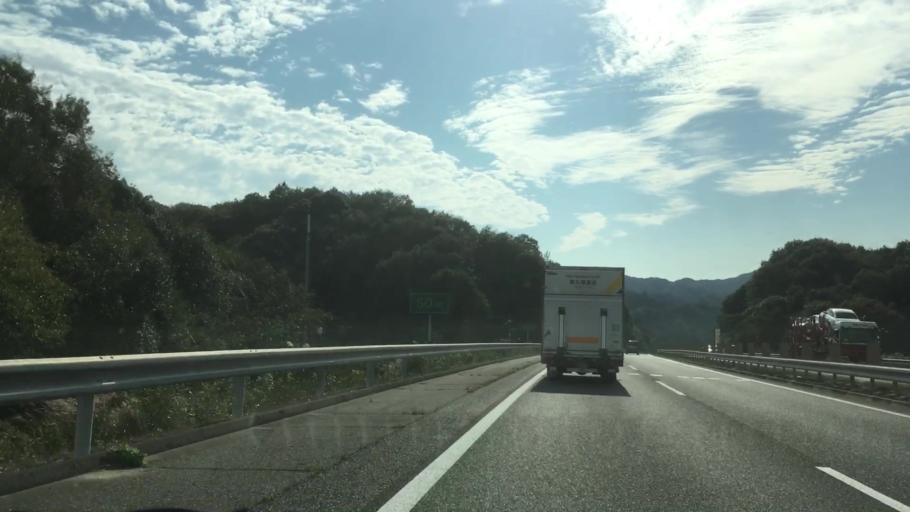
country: JP
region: Yamaguchi
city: Yanai
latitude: 34.0701
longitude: 132.0635
